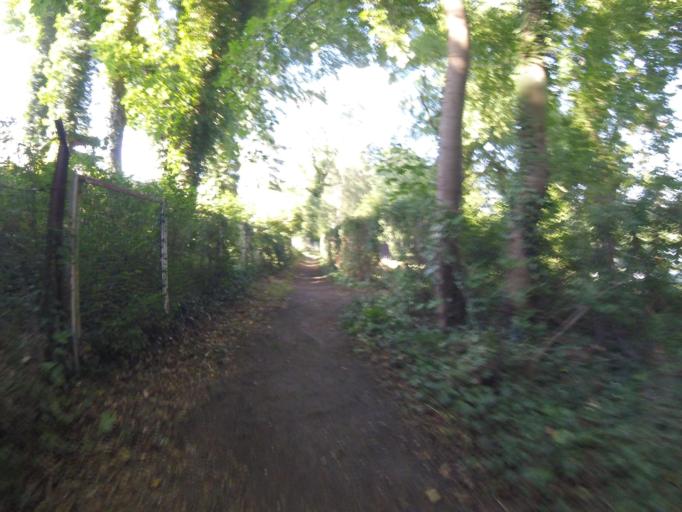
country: DE
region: Brandenburg
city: Wildau
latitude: 52.3081
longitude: 13.7046
